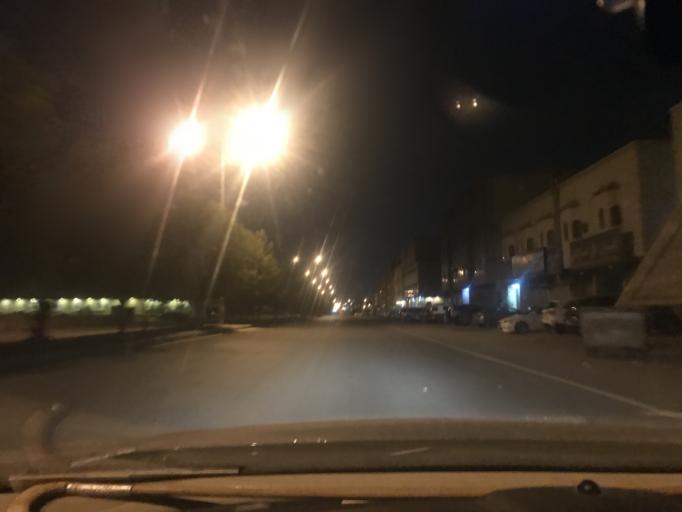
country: SA
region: Ar Riyad
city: Riyadh
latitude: 24.7564
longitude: 46.7552
